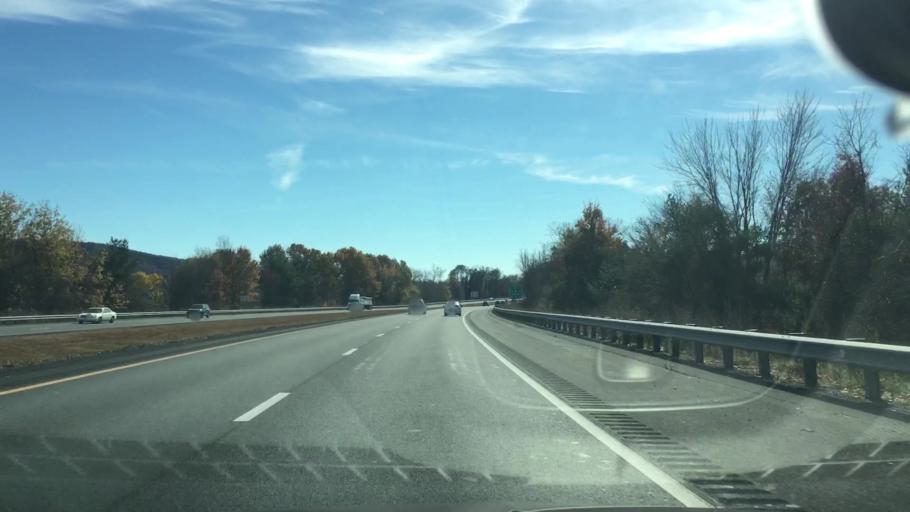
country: US
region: Massachusetts
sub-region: Hampshire County
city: Northampton
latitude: 42.3254
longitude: -72.6161
